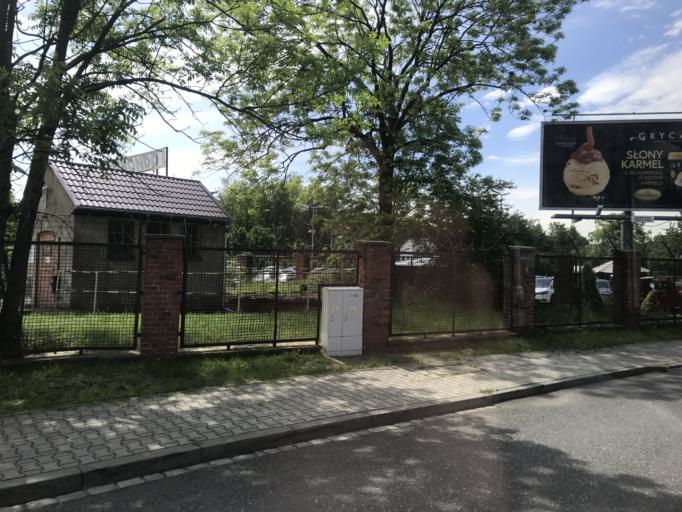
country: PL
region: Lower Silesian Voivodeship
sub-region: Powiat wroclawski
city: Smolec
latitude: 51.1094
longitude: 16.9031
